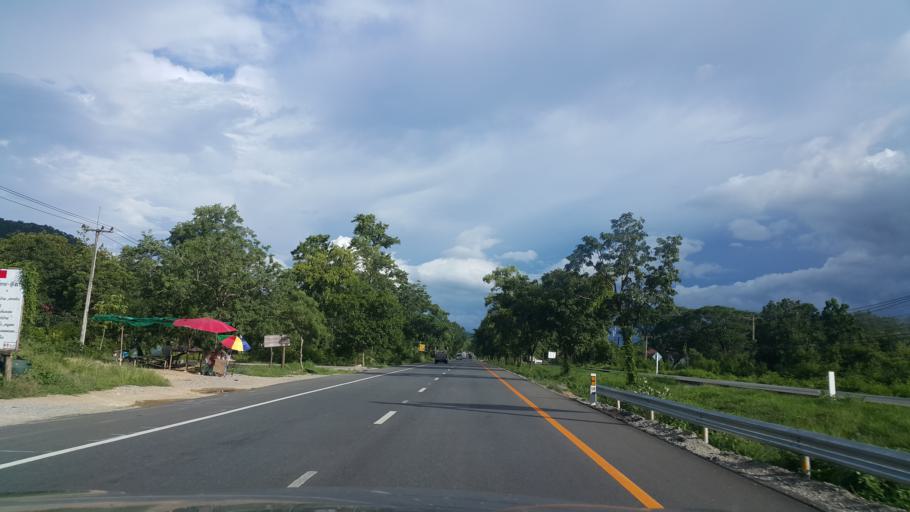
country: TH
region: Tak
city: Ban Tak
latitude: 17.0055
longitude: 99.1097
